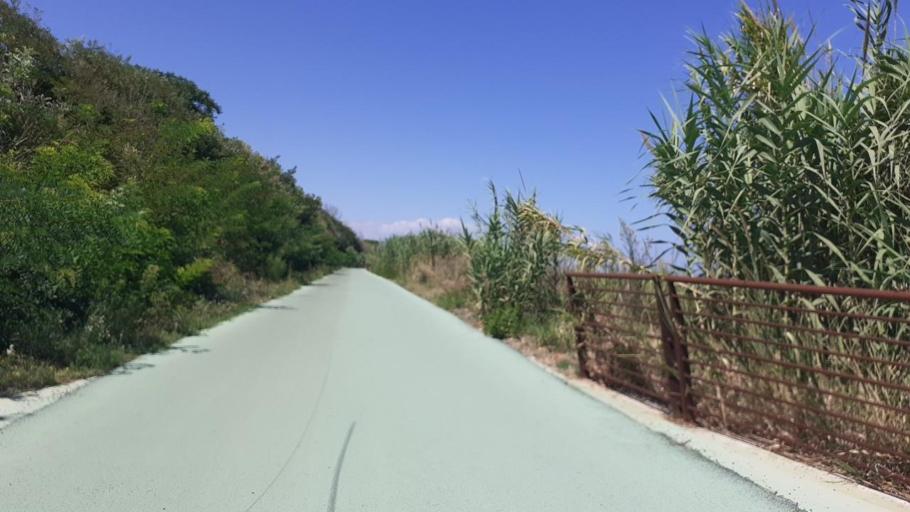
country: IT
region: Abruzzo
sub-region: Provincia di Chieti
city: Torino di Sangro
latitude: 42.2126
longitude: 14.5866
